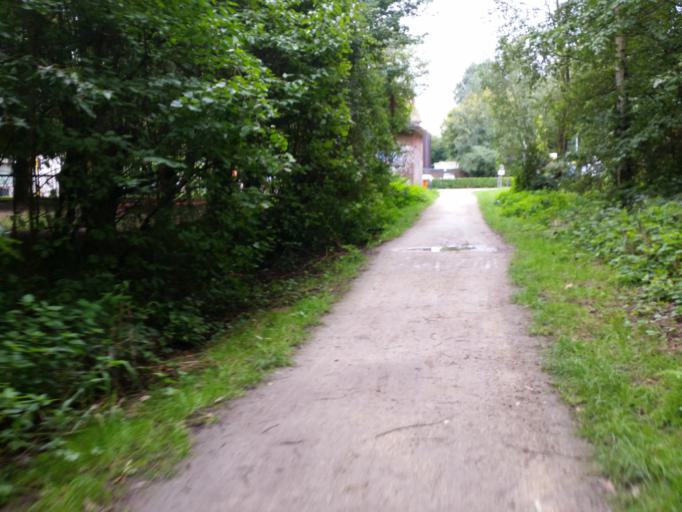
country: BE
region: Flanders
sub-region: Provincie Antwerpen
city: Kontich
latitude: 51.1289
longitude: 4.4424
